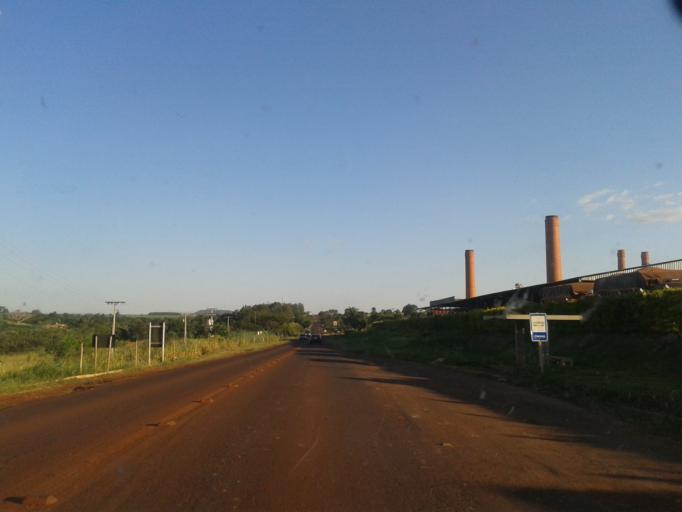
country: BR
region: Minas Gerais
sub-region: Capinopolis
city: Capinopolis
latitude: -18.6908
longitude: -49.5626
